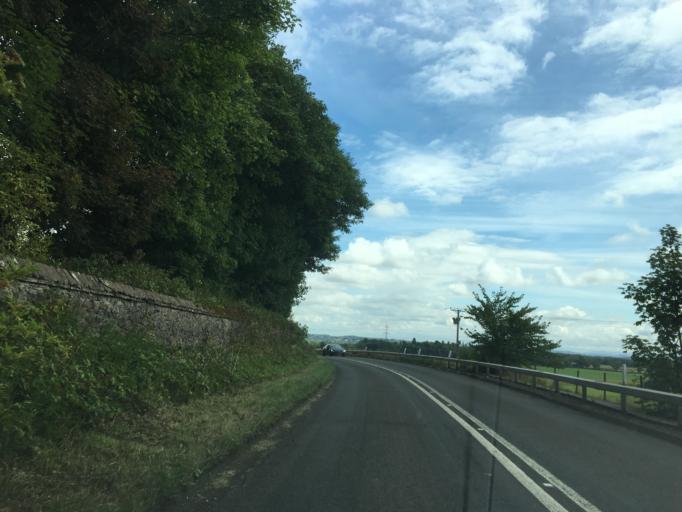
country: GB
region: Scotland
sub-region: Stirling
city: Stirling
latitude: 56.1416
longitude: -3.9123
